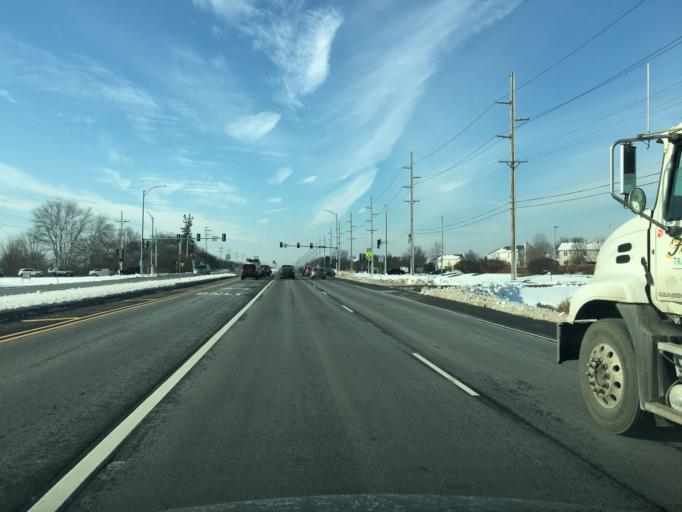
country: US
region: Illinois
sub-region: DuPage County
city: Naperville
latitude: 41.7474
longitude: -88.1849
